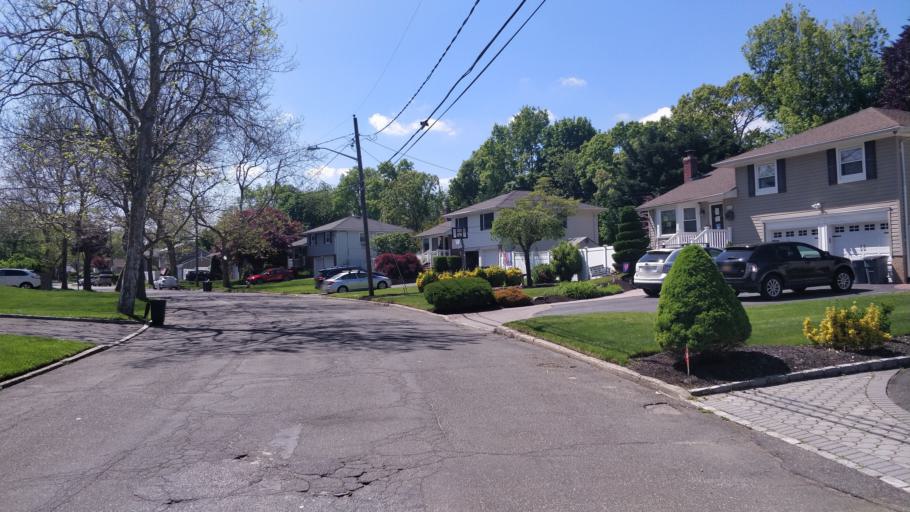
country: US
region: New York
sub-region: Suffolk County
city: Commack
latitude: 40.8454
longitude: -73.3060
